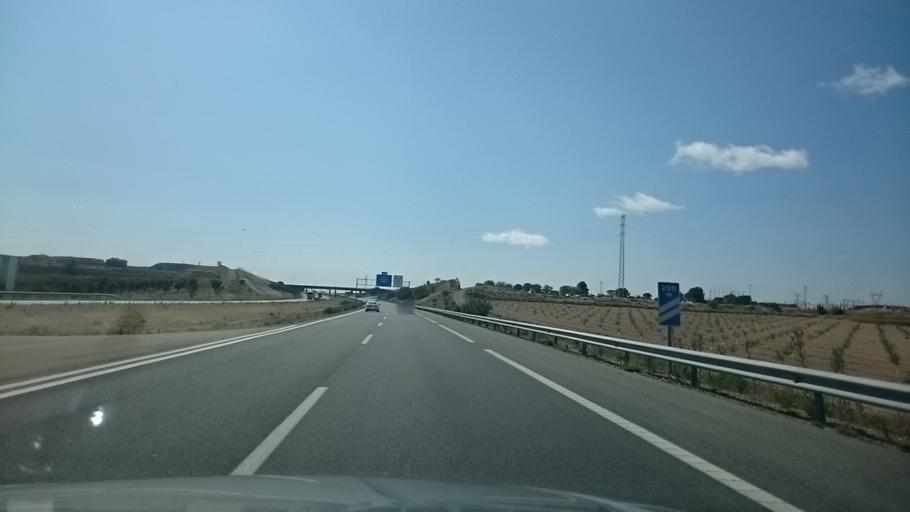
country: ES
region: Aragon
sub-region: Provincia de Zaragoza
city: Mallen
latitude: 41.8562
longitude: -1.3833
